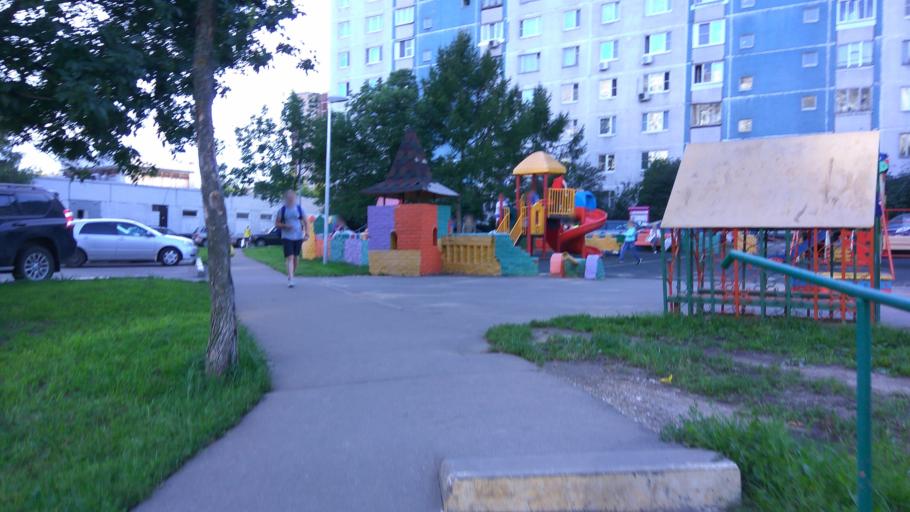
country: RU
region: Moscow
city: Tsaritsyno
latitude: 55.6253
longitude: 37.6677
